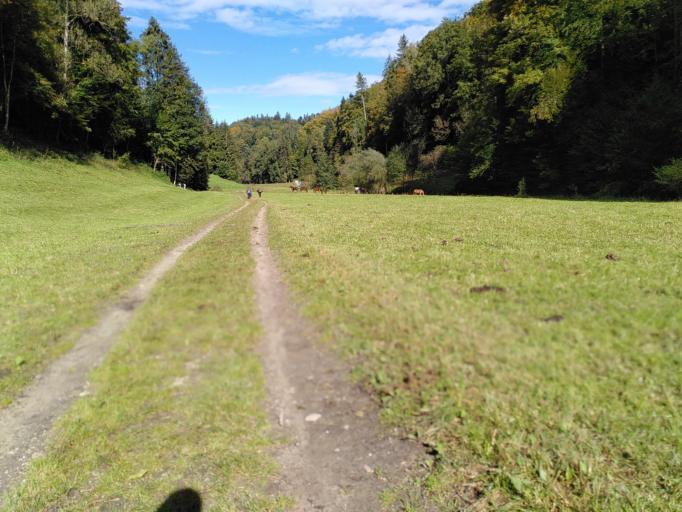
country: CH
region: Bern
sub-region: Oberaargau
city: Seeberg
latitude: 47.1324
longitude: 7.7034
